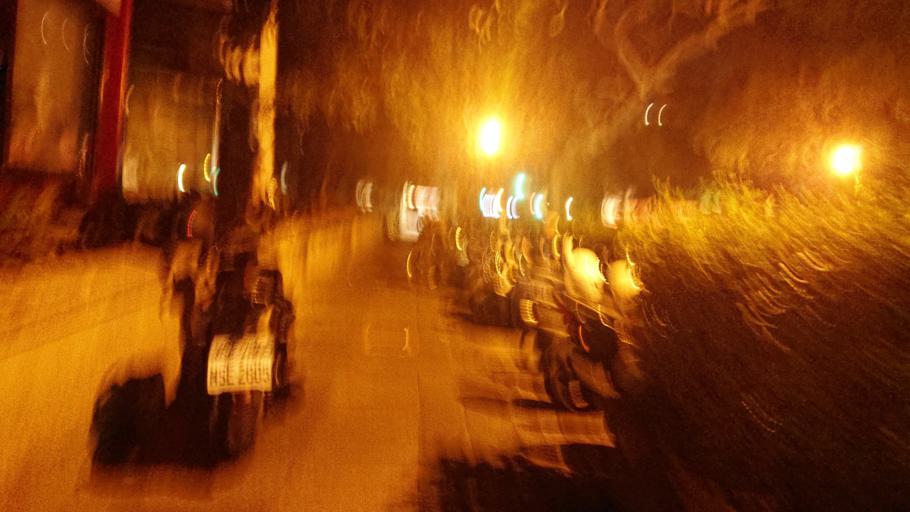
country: TW
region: Taiwan
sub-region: Tainan
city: Tainan
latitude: 22.9907
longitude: 120.2050
